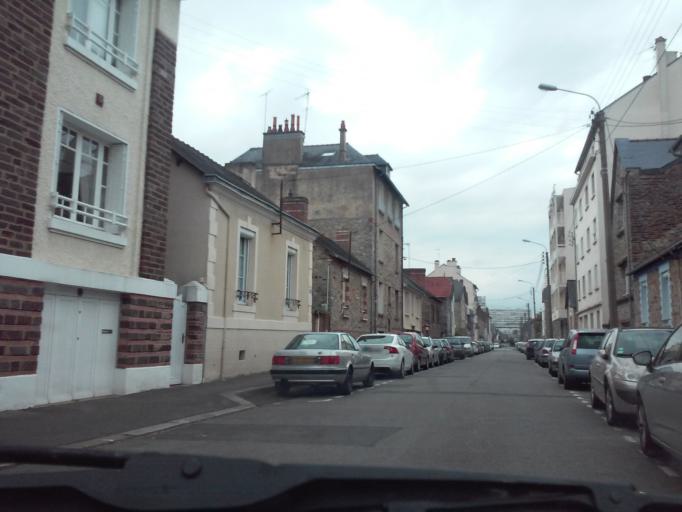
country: FR
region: Brittany
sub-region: Departement d'Ille-et-Vilaine
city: Rennes
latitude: 48.0977
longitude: -1.6790
